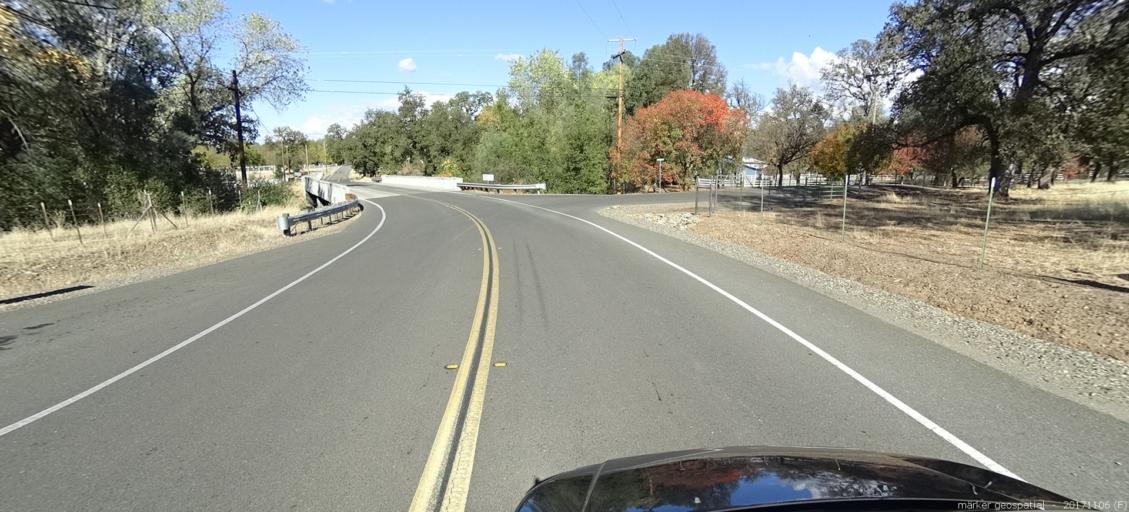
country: US
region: California
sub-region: Shasta County
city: Palo Cedro
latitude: 40.5856
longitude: -122.2230
